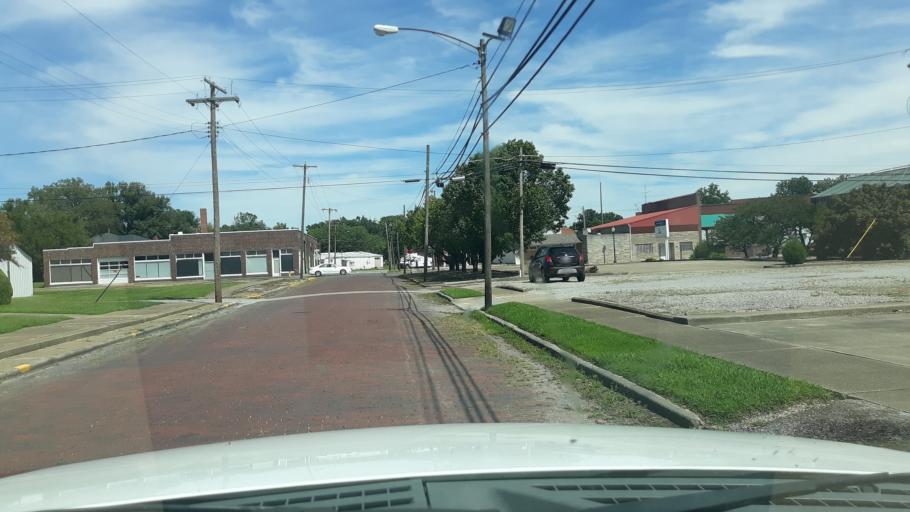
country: US
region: Illinois
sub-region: Saline County
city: Eldorado
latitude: 37.8140
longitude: -88.4399
